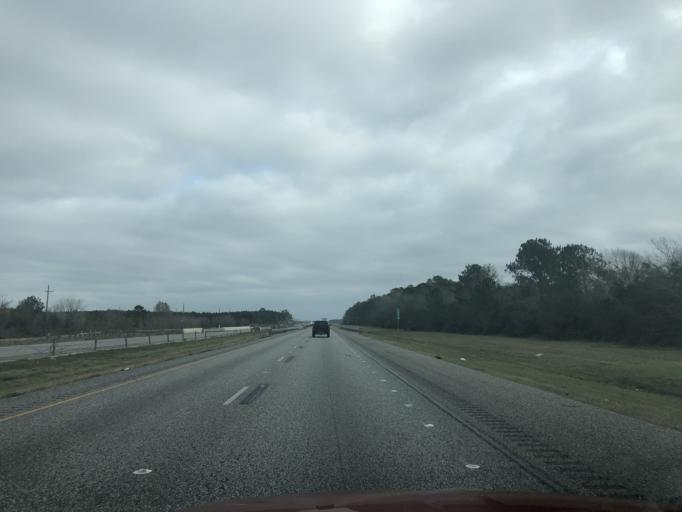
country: US
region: Texas
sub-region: Jefferson County
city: Fannett
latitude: 29.8863
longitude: -94.3241
